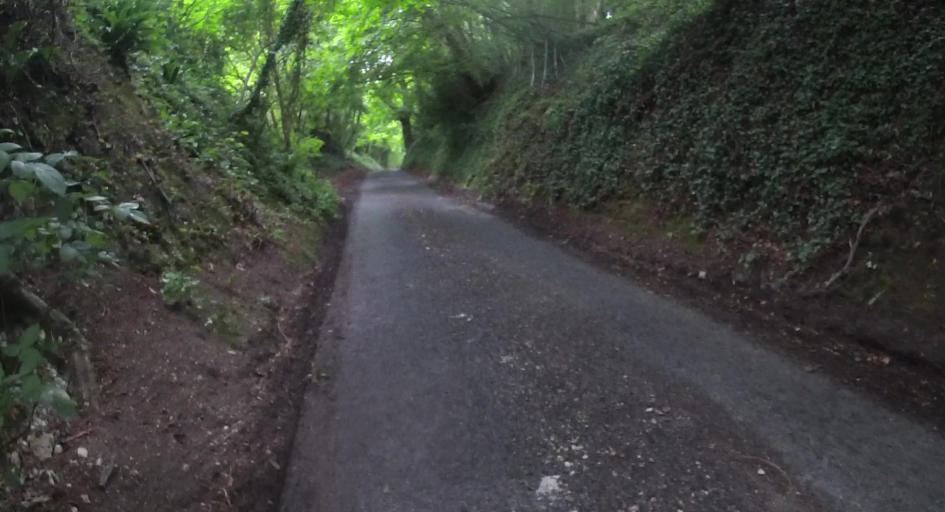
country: GB
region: England
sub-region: Hampshire
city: Long Sutton
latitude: 51.1985
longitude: -0.9140
